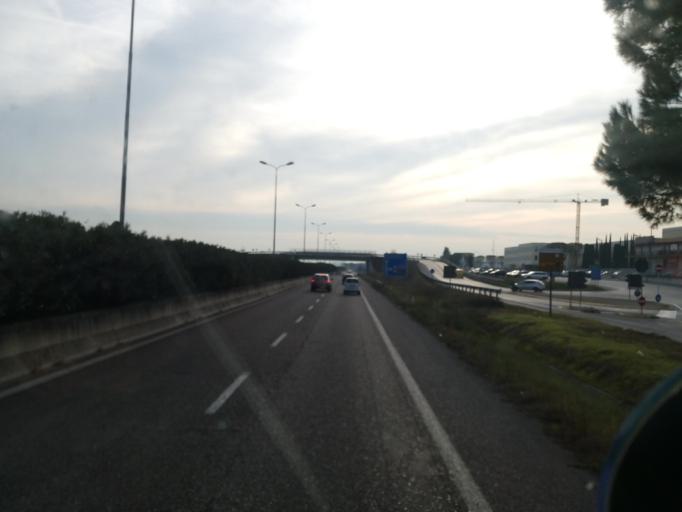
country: IT
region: Lombardy
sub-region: Provincia di Brescia
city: Desenzano del Garda
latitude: 45.4463
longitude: 10.5201
